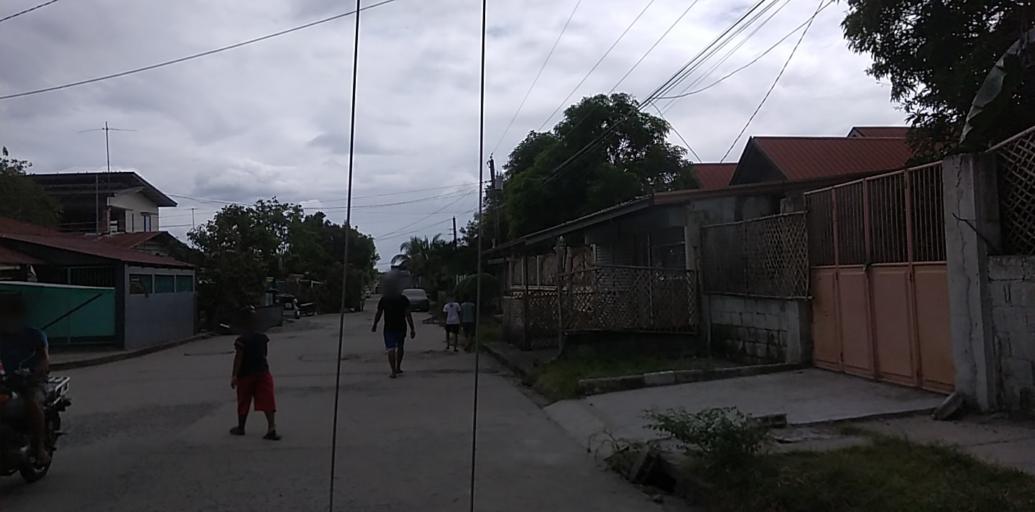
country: PH
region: Central Luzon
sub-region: Province of Pampanga
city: Pio
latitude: 15.0448
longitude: 120.5261
